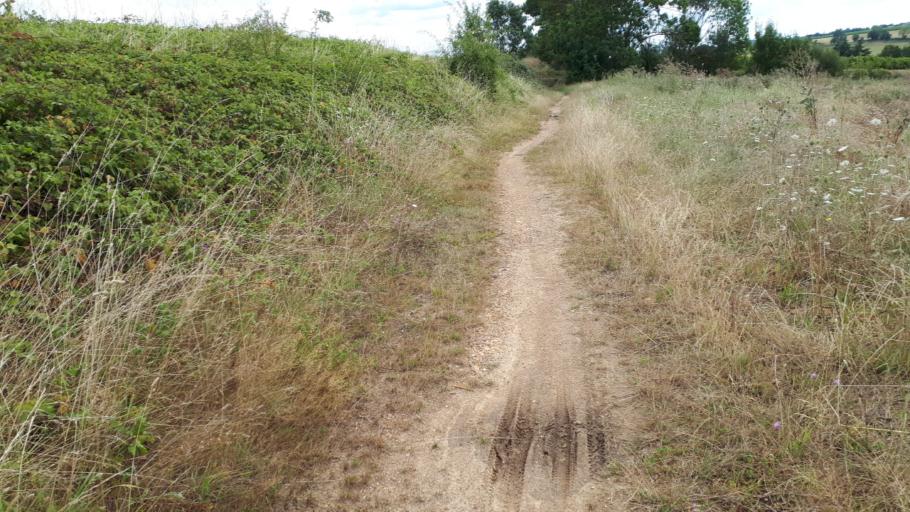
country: FR
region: Pays de la Loire
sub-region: Departement de Maine-et-Loire
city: Rochefort-sur-Loire
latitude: 47.3290
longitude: -0.6840
